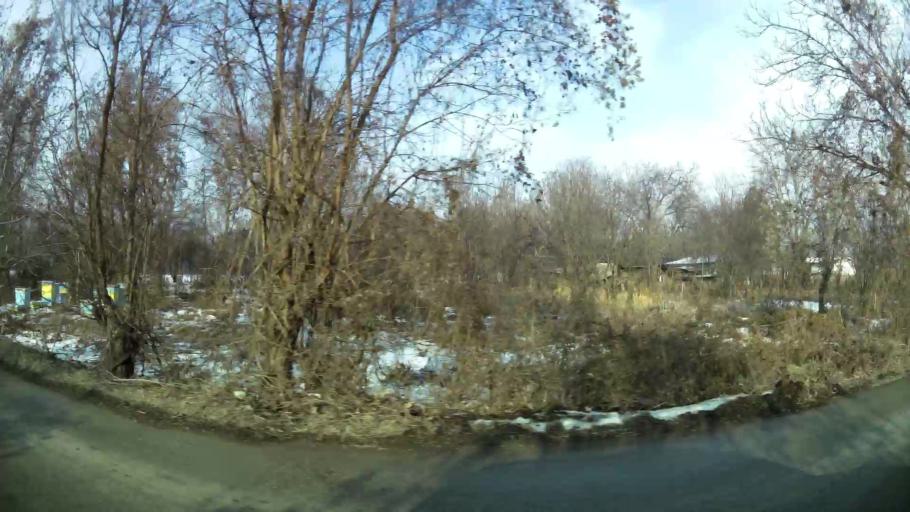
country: MK
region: Ilinden
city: Jurumleri
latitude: 41.9914
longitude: 21.5294
